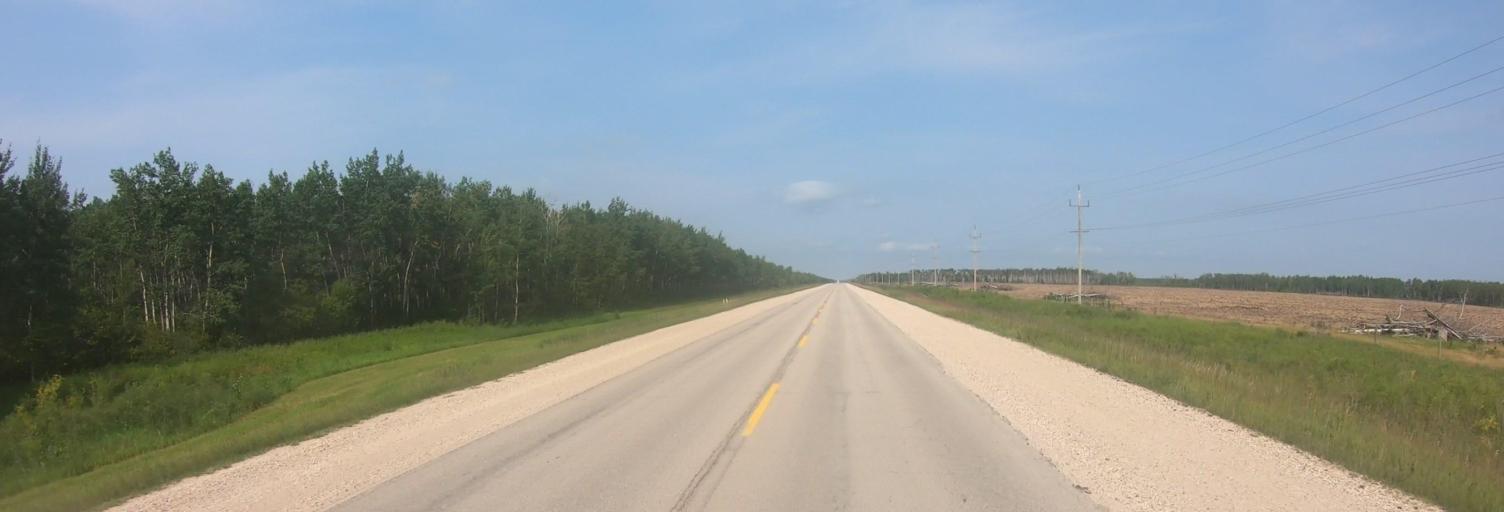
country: CA
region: Manitoba
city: Steinbach
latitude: 49.3314
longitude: -96.6100
